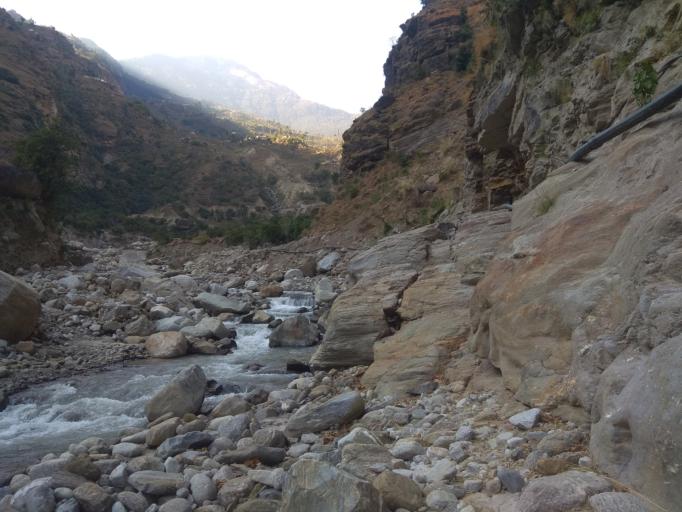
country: NP
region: Far Western
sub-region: Seti Zone
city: Achham
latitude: 29.2286
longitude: 81.6227
